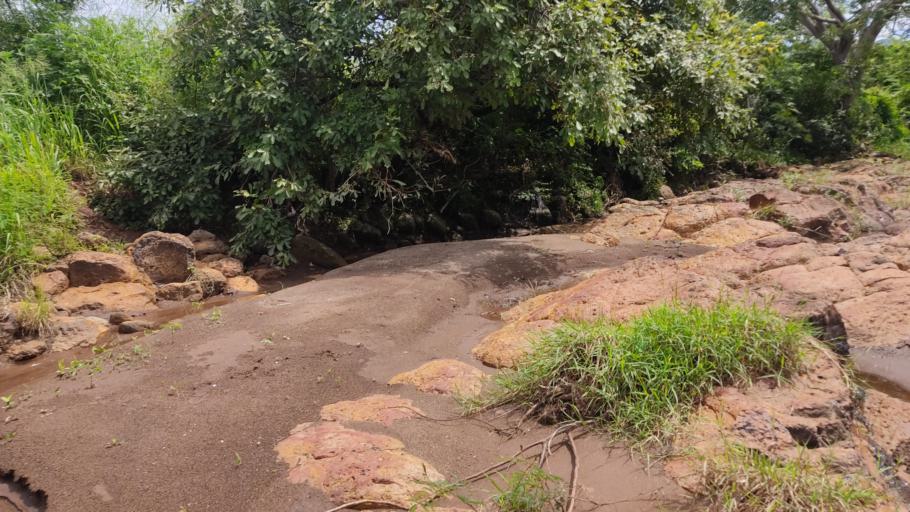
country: MX
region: Nayarit
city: Puga
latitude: 21.6668
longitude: -104.8518
